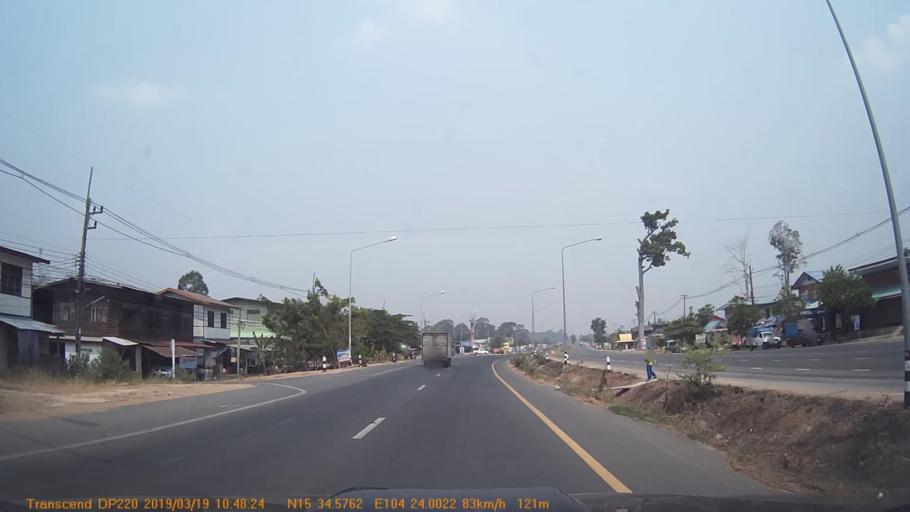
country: TH
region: Yasothon
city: Kham Khuean Kaeo
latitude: 15.5766
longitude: 104.3998
